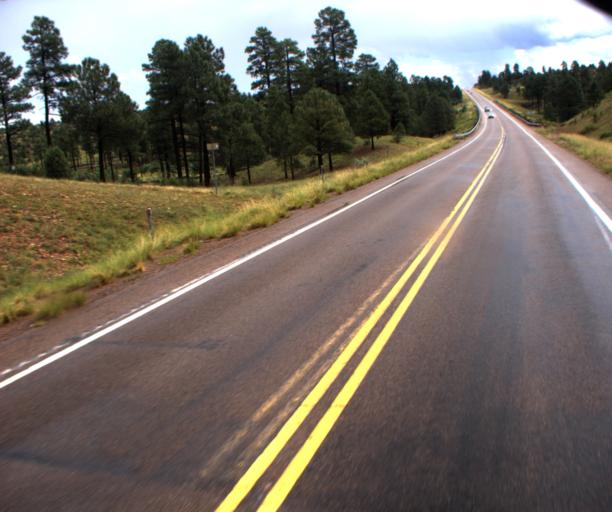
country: US
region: Arizona
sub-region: Navajo County
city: Heber-Overgaard
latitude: 34.3679
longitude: -110.3892
